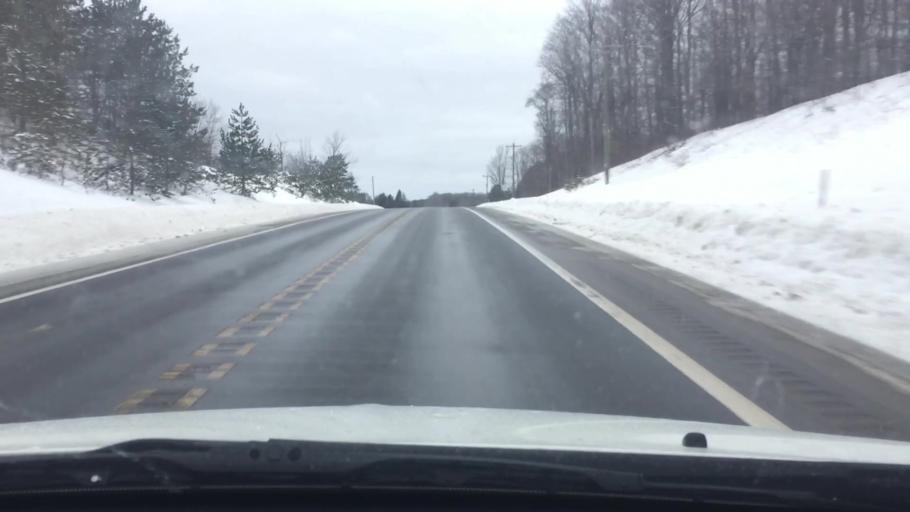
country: US
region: Michigan
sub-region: Charlevoix County
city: Boyne City
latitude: 45.0963
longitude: -85.0113
